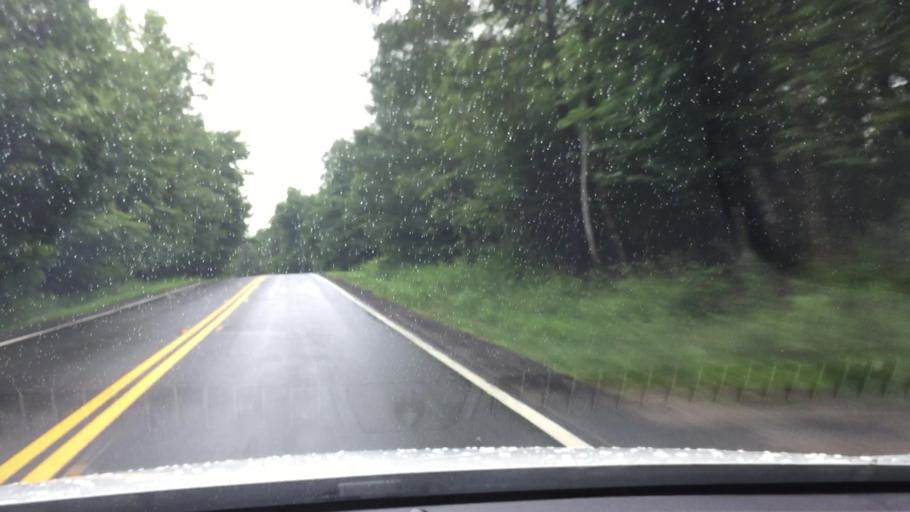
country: US
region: Massachusetts
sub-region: Berkshire County
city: Hinsdale
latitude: 42.3696
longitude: -73.1458
